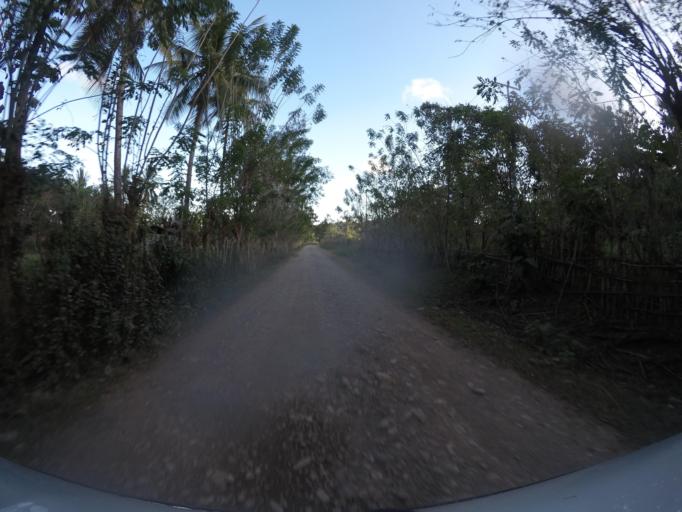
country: TL
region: Baucau
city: Venilale
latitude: -8.7267
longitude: 126.7086
